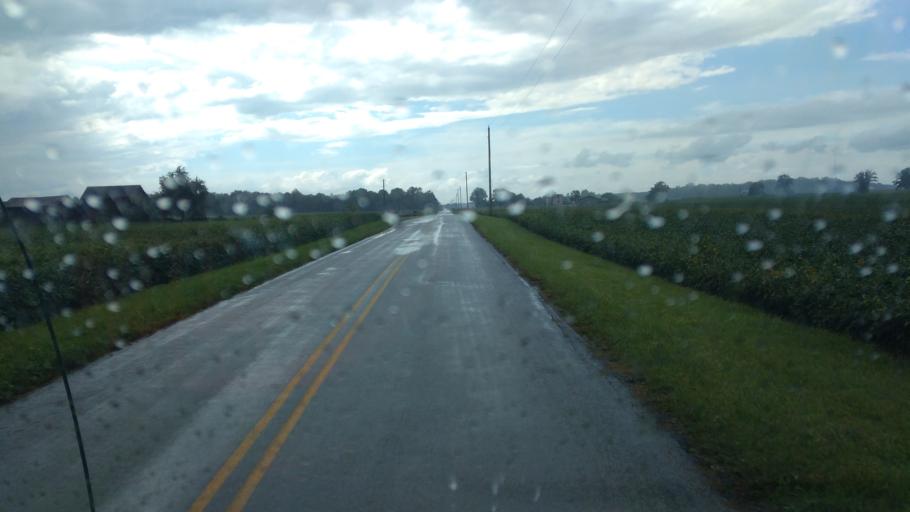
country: US
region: Ohio
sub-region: Hardin County
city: Kenton
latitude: 40.7034
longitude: -83.6063
